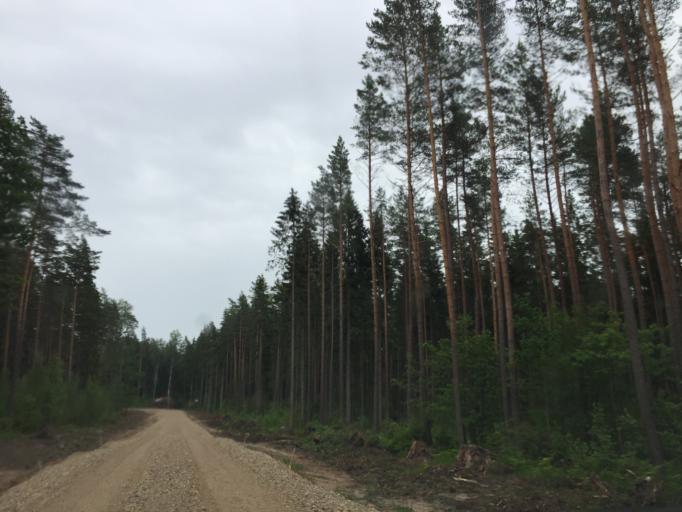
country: LV
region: Tukuma Rajons
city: Tukums
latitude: 57.0042
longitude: 23.1080
